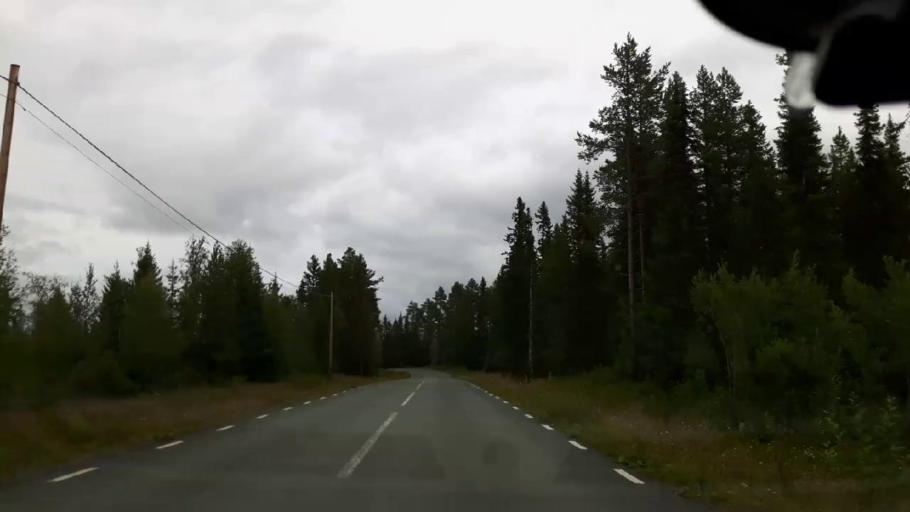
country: SE
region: Jaemtland
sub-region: Krokoms Kommun
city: Valla
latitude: 63.6641
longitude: 13.8549
